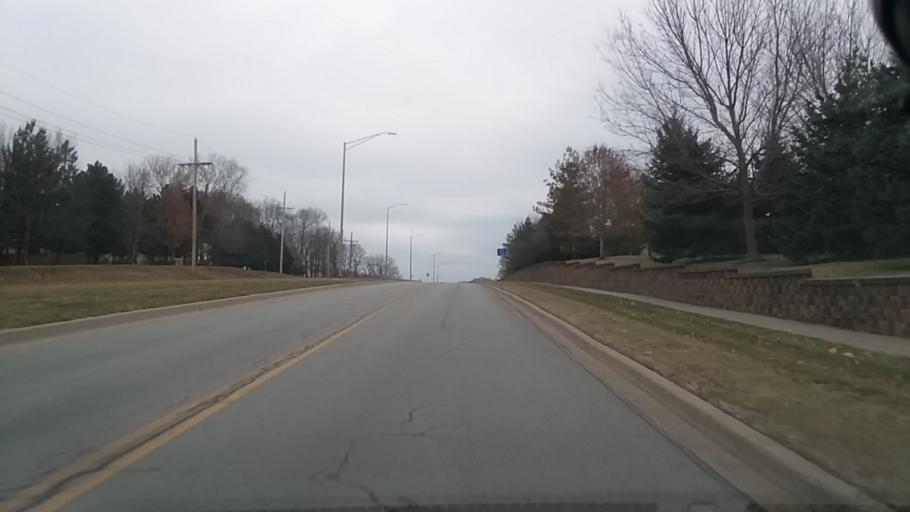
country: US
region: Kansas
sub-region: Johnson County
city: Olathe
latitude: 38.9127
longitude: -94.8277
